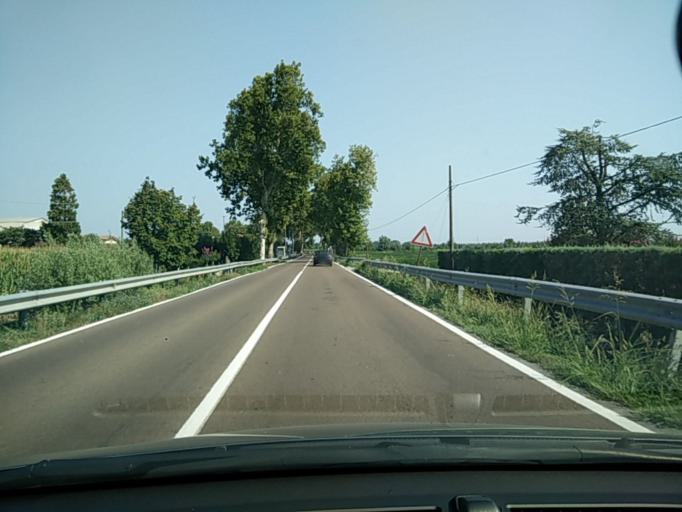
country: IT
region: Veneto
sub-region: Provincia di Venezia
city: San Giorgio di Livenza
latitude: 45.6487
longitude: 12.7747
